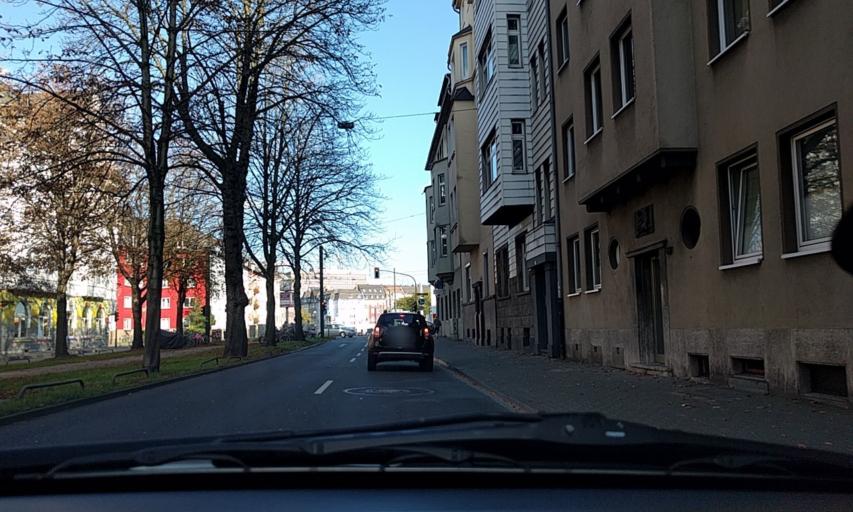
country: DE
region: North Rhine-Westphalia
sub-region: Regierungsbezirk Dusseldorf
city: Dusseldorf
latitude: 51.2023
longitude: 6.7796
